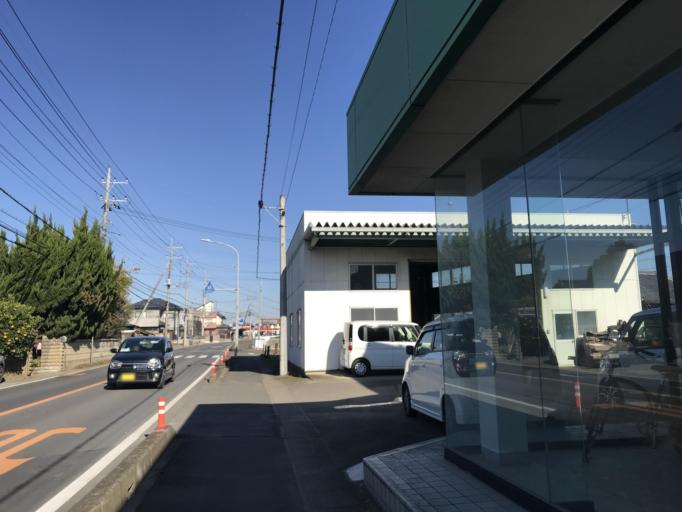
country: JP
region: Ibaraki
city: Yuki
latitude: 36.2850
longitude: 139.8578
